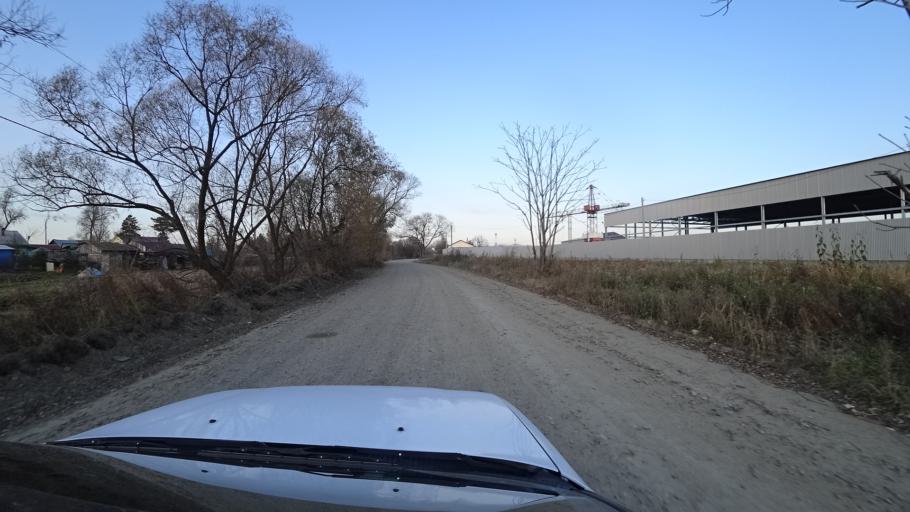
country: RU
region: Primorskiy
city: Dal'nerechensk
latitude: 45.9421
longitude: 133.8235
